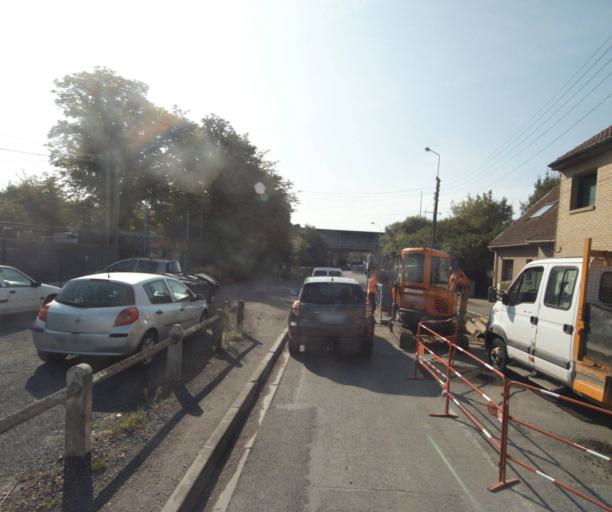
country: FR
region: Nord-Pas-de-Calais
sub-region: Departement du Nord
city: Wambrechies
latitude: 50.6809
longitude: 3.0543
